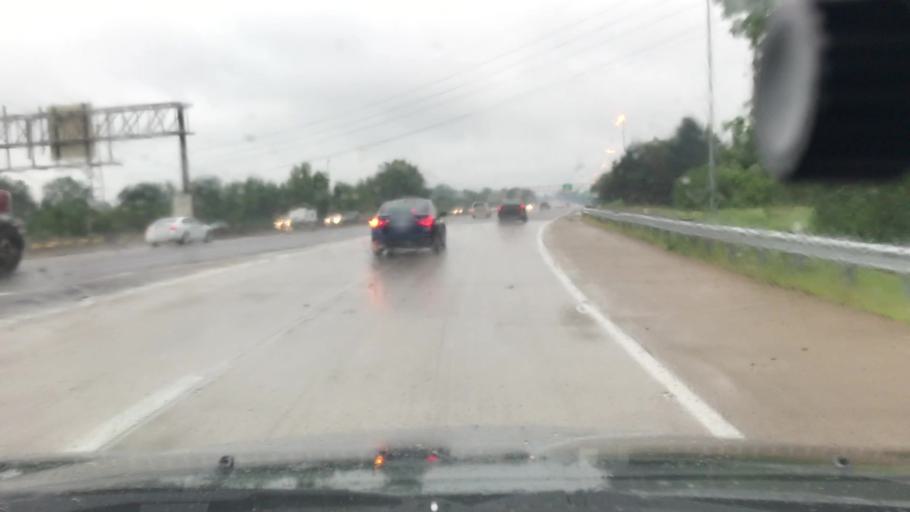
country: US
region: Missouri
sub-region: Saint Louis County
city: Creve Coeur
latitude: 38.6424
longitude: -90.4490
